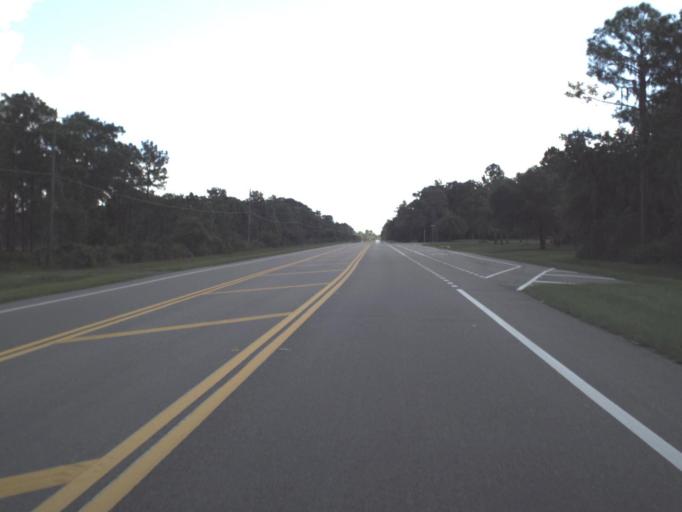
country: US
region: Florida
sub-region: Sarasota County
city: The Meadows
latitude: 27.4071
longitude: -82.3266
